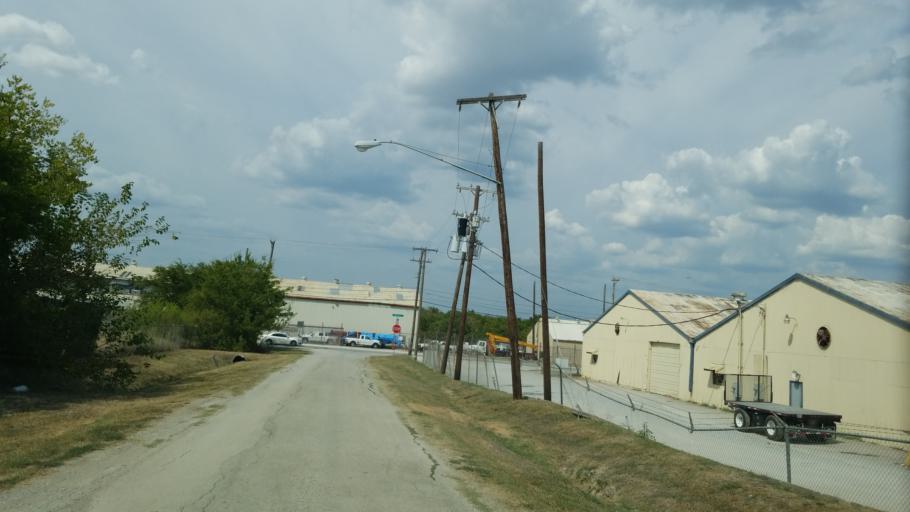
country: US
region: Texas
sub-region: Dallas County
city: Dallas
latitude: 32.7716
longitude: -96.8458
